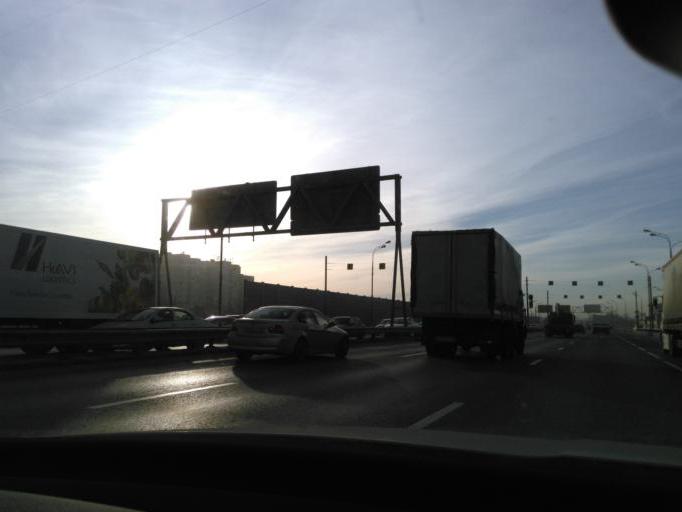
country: RU
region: Moscow
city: Lefortovo
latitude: 55.7343
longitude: 37.7007
